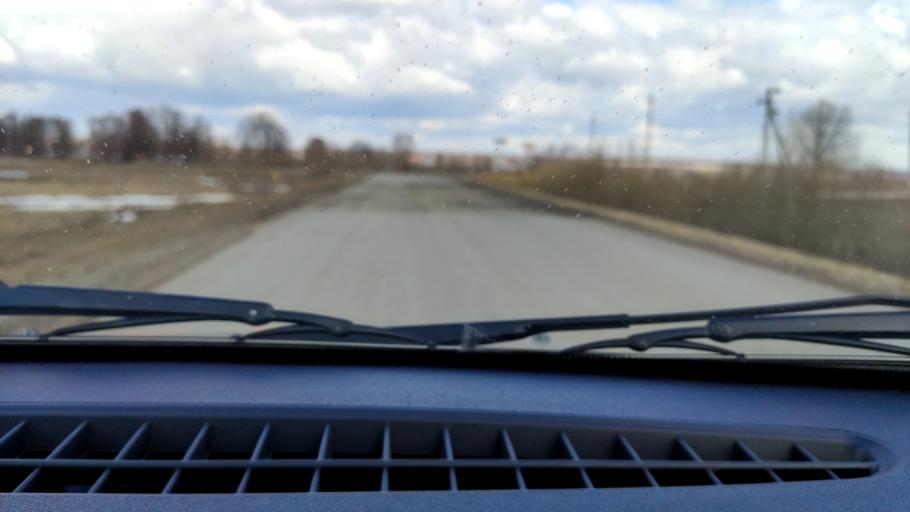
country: RU
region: Bashkortostan
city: Kudeyevskiy
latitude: 54.8497
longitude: 56.7955
